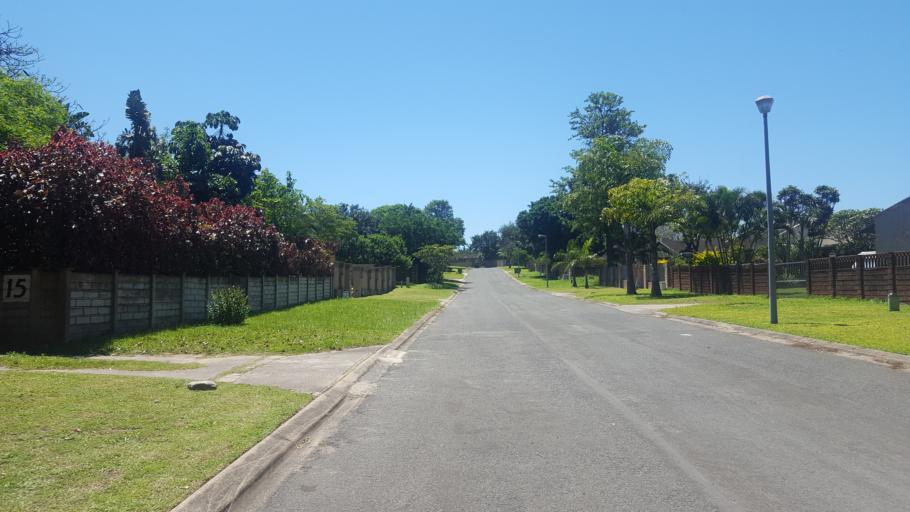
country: ZA
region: KwaZulu-Natal
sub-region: uThungulu District Municipality
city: Richards Bay
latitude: -28.7657
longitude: 32.0641
